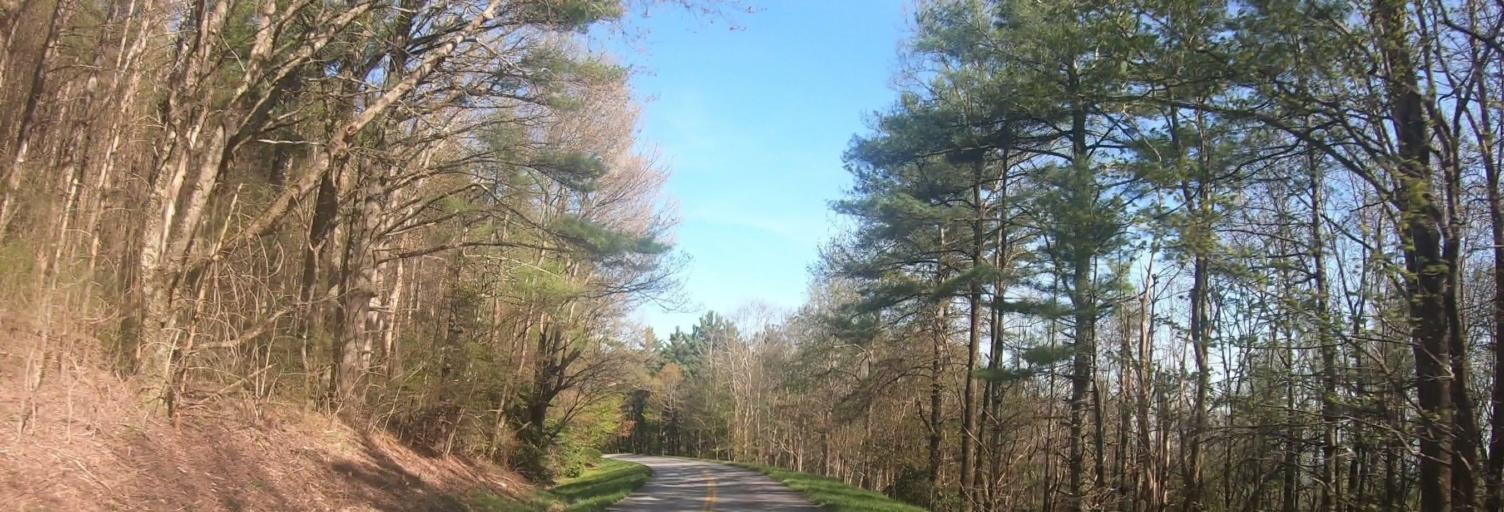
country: US
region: North Carolina
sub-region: Watauga County
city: Boone
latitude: 36.2214
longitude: -81.5082
